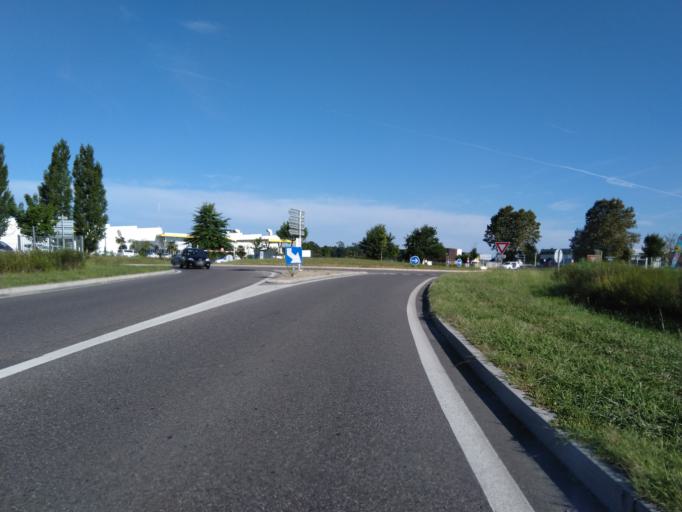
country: FR
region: Aquitaine
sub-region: Departement des Landes
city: Saint-Vincent-de-Paul
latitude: 43.7400
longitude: -1.0177
